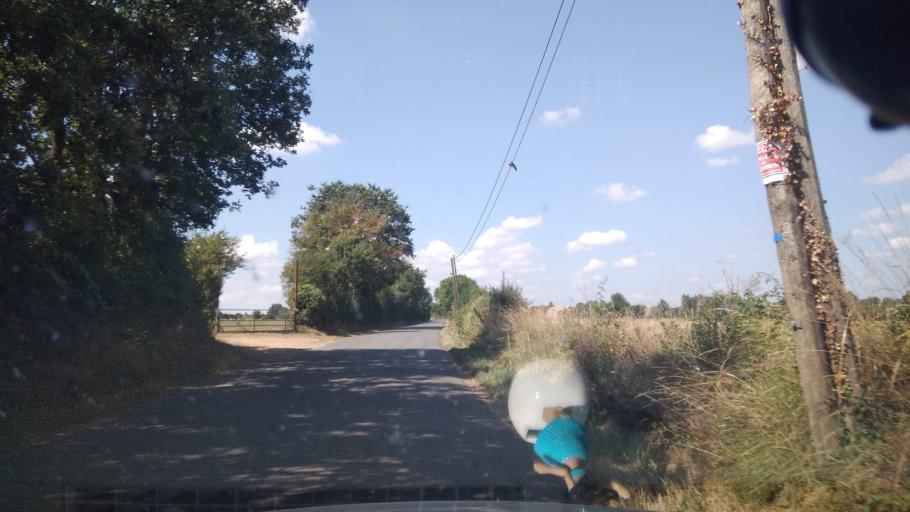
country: FR
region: Poitou-Charentes
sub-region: Departement de la Vienne
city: Ayron
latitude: 46.6538
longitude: 0.0716
